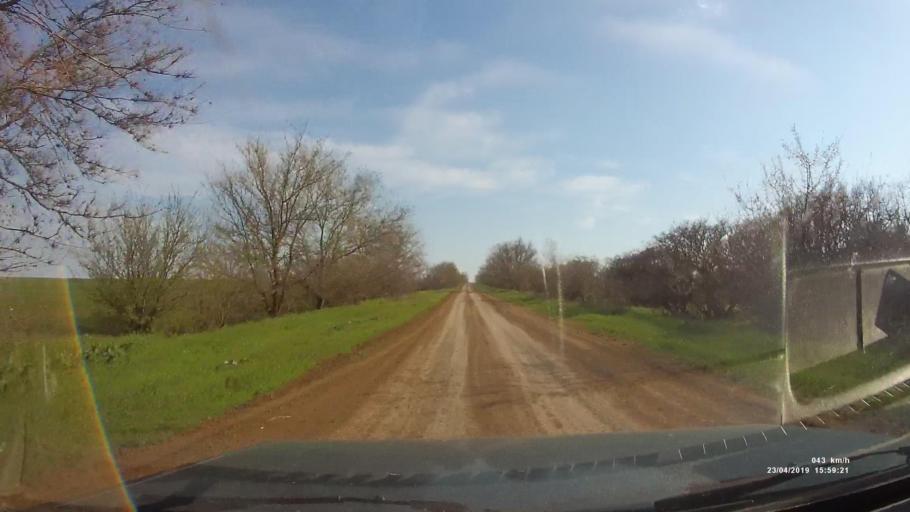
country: RU
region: Rostov
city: Remontnoye
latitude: 46.5174
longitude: 43.1096
